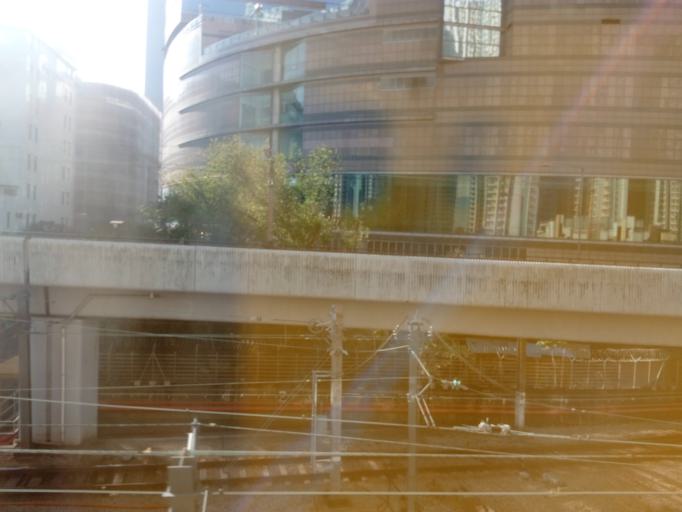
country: HK
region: Kowloon City
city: Kowloon
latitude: 22.3208
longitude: 114.2139
